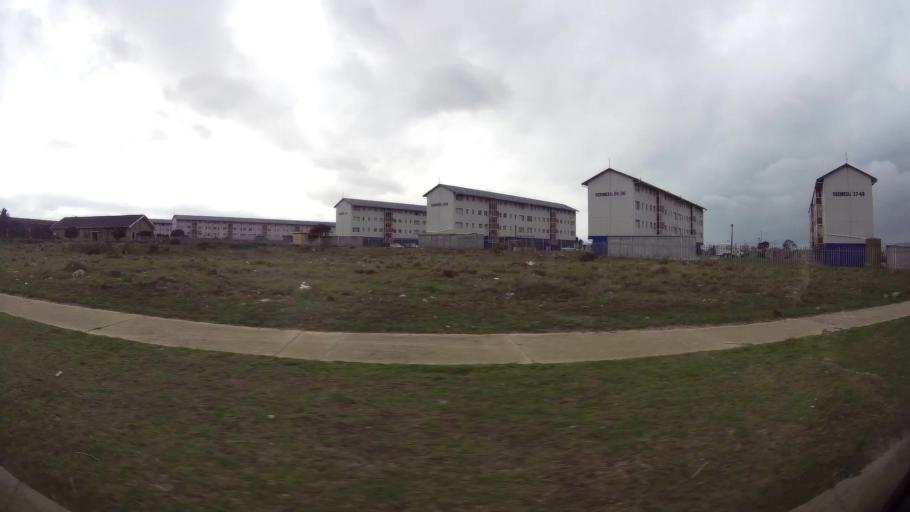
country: ZA
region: Eastern Cape
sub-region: Nelson Mandela Bay Metropolitan Municipality
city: Port Elizabeth
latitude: -33.9031
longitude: 25.5554
